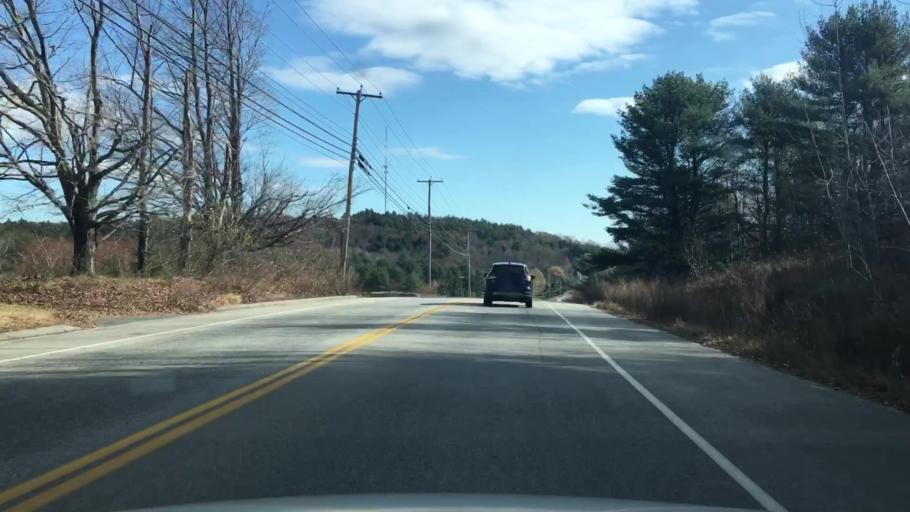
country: US
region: Maine
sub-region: Kennebec County
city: Augusta
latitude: 44.3032
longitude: -69.7408
